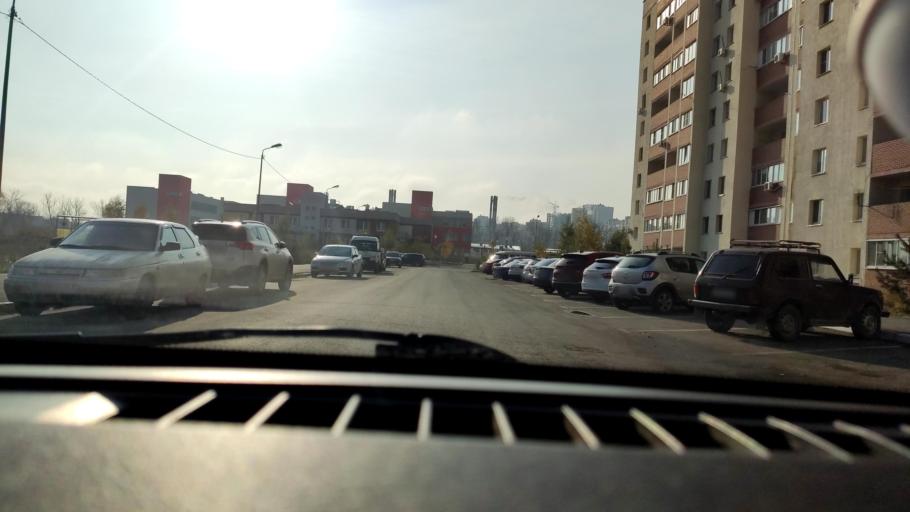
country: RU
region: Samara
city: Samara
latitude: 53.1567
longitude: 50.0794
